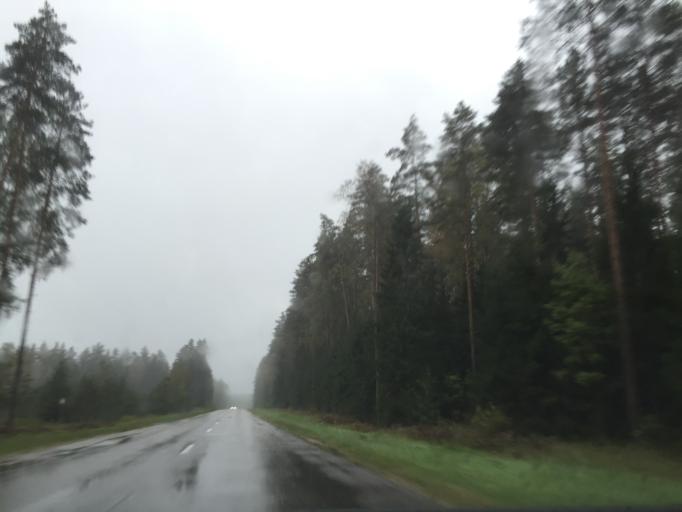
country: LV
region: Ropazu
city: Ropazi
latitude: 57.0190
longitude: 24.6832
